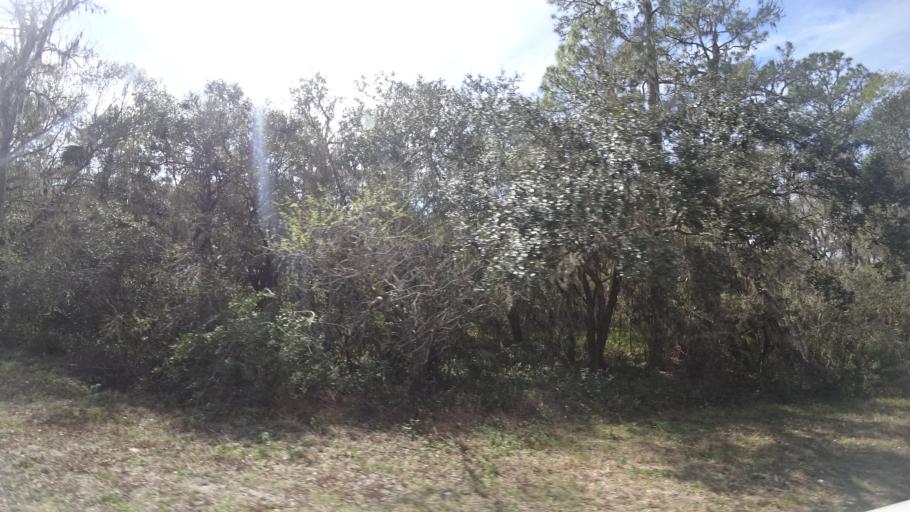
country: US
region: Florida
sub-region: Manatee County
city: Ellenton
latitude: 27.5723
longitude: -82.3866
